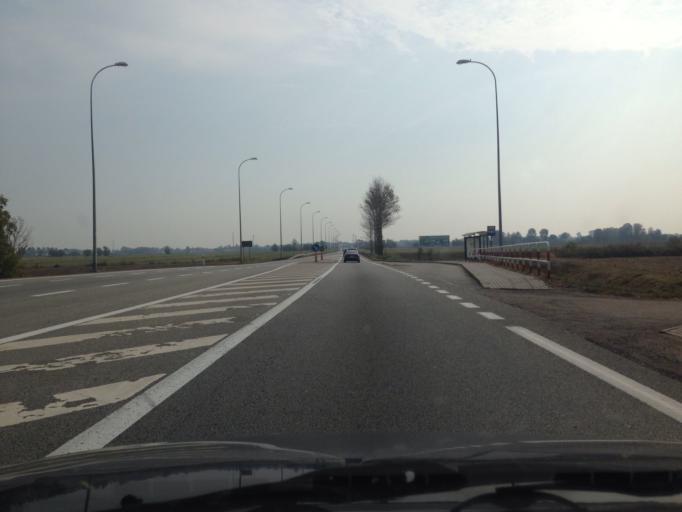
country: PL
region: Pomeranian Voivodeship
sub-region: Powiat nowodworski
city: Nowy Dwor Gdanski
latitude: 54.2199
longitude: 19.0787
